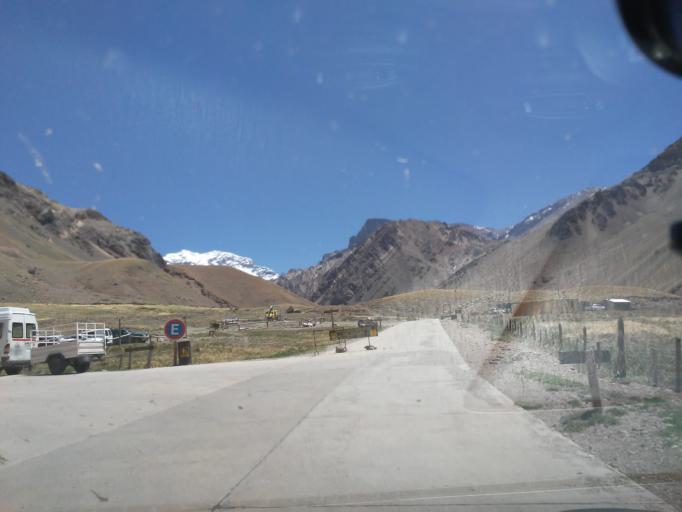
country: CL
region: Valparaiso
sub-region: Provincia de Los Andes
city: Los Andes
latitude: -32.8120
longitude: -69.9425
